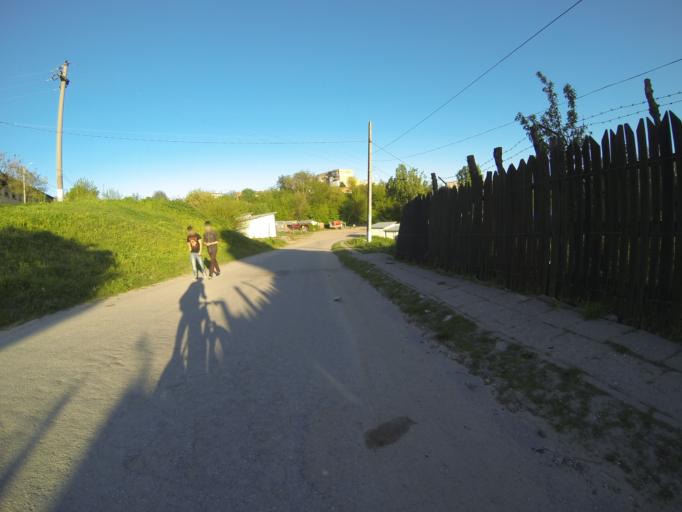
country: RO
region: Dolj
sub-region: Comuna Segarcea
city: Segarcea
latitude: 44.0954
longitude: 23.7433
